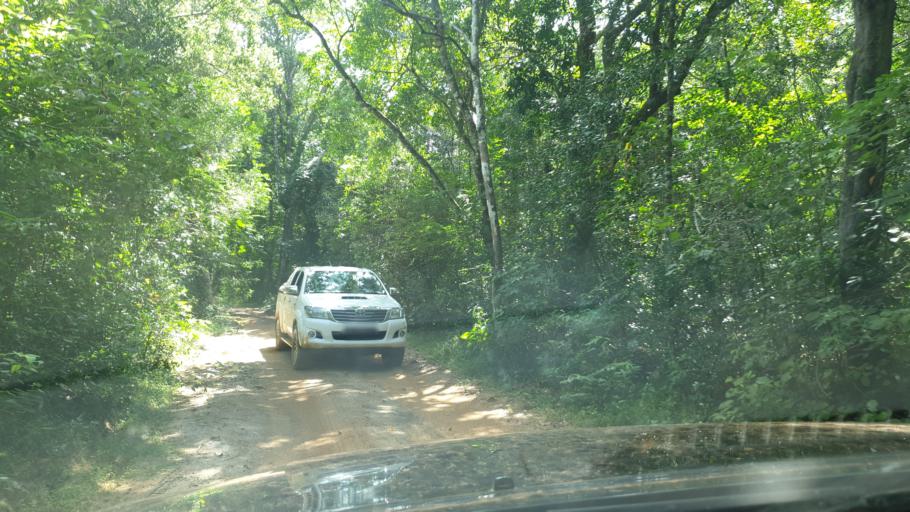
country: LK
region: North Central
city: Anuradhapura
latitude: 8.4224
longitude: 80.0235
